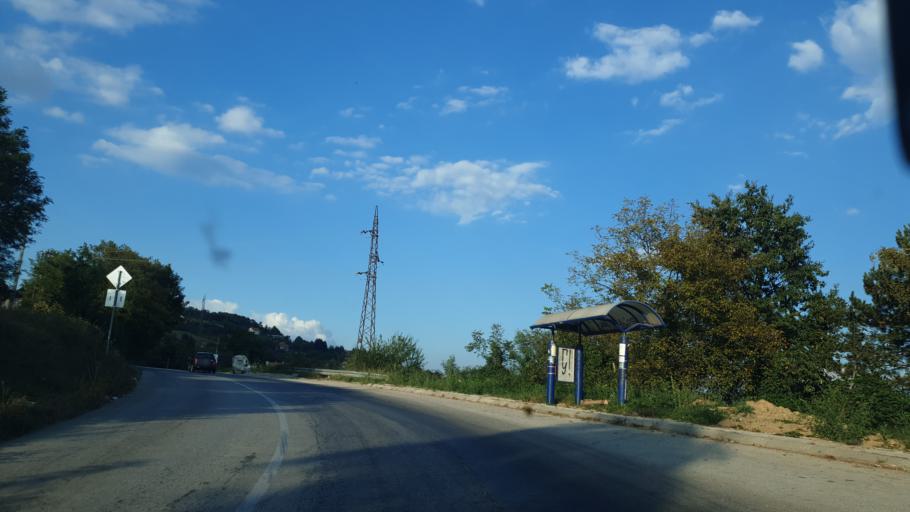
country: RS
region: Central Serbia
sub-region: Zlatiborski Okrug
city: Uzice
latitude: 43.8576
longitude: 19.8769
